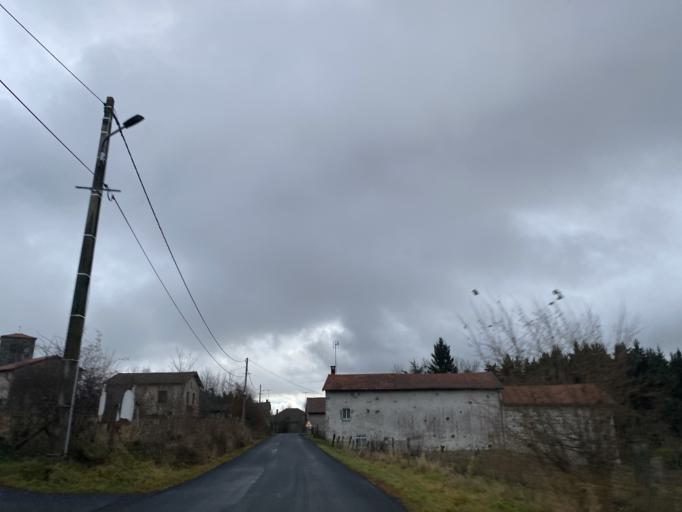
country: FR
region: Auvergne
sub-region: Departement du Puy-de-Dome
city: Cunlhat
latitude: 45.5617
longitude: 3.5727
